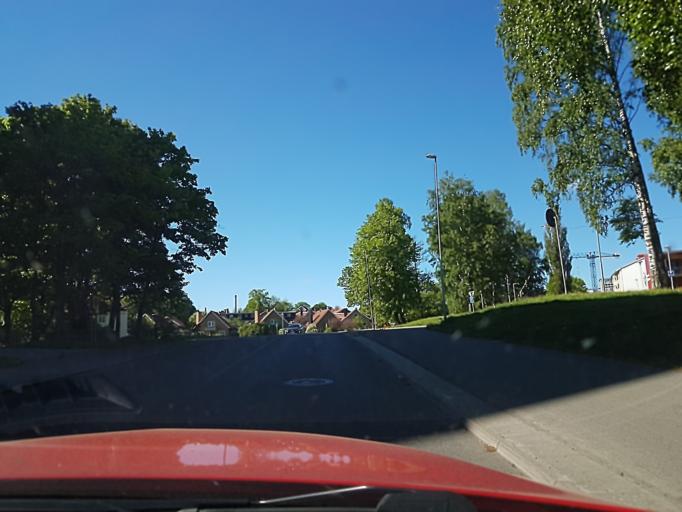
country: SE
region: Vaestra Goetaland
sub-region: Skovde Kommun
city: Skoevde
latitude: 58.3902
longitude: 13.8630
